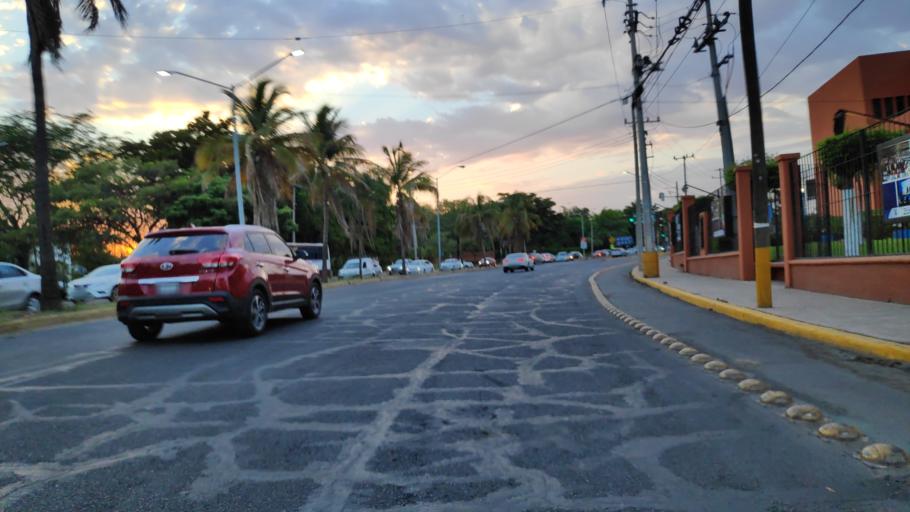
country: MX
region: Sinaloa
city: Culiacan
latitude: 24.8211
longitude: -107.3829
